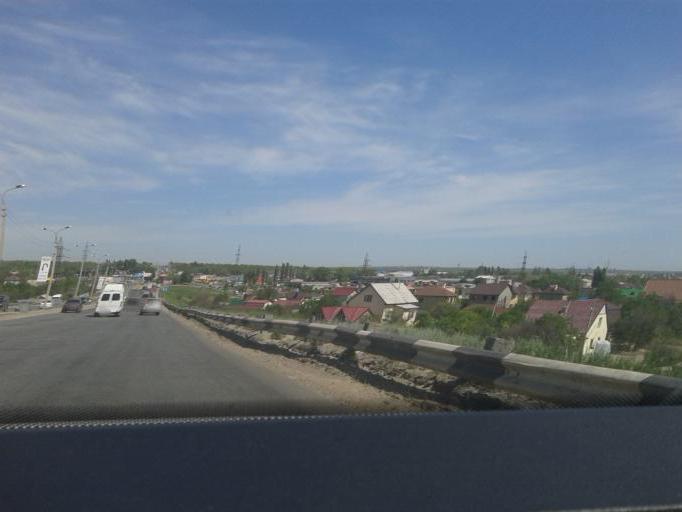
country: RU
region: Volgograd
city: Volgograd
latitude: 48.7706
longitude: 44.5194
